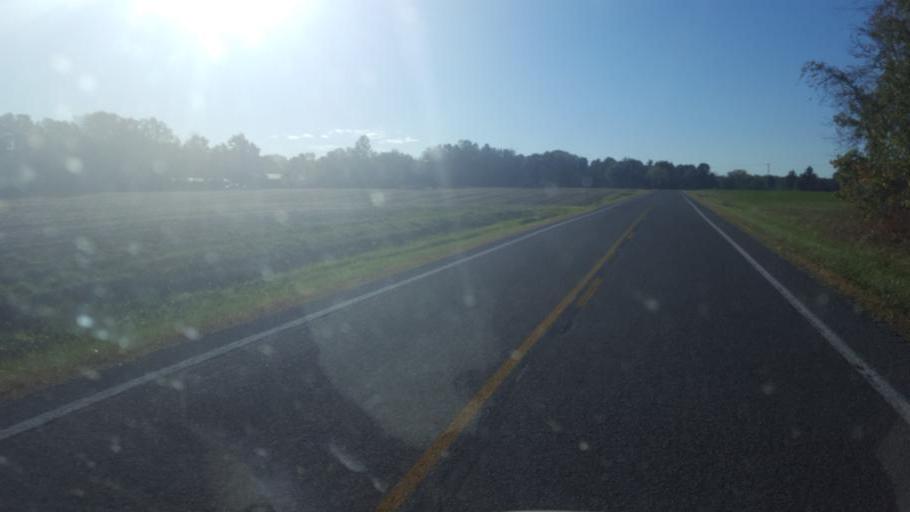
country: US
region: Ohio
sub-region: Crawford County
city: Galion
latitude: 40.6927
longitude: -82.8633
